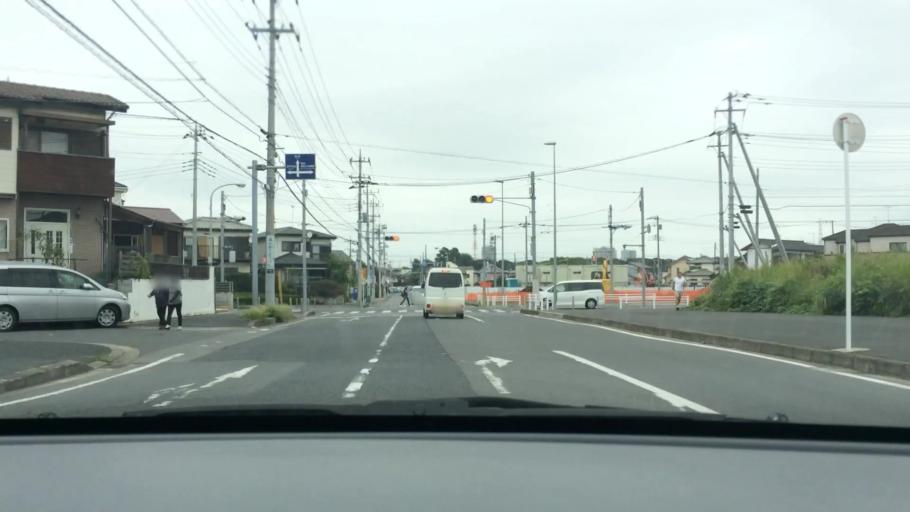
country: JP
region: Chiba
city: Nagareyama
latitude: 35.8813
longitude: 139.9245
